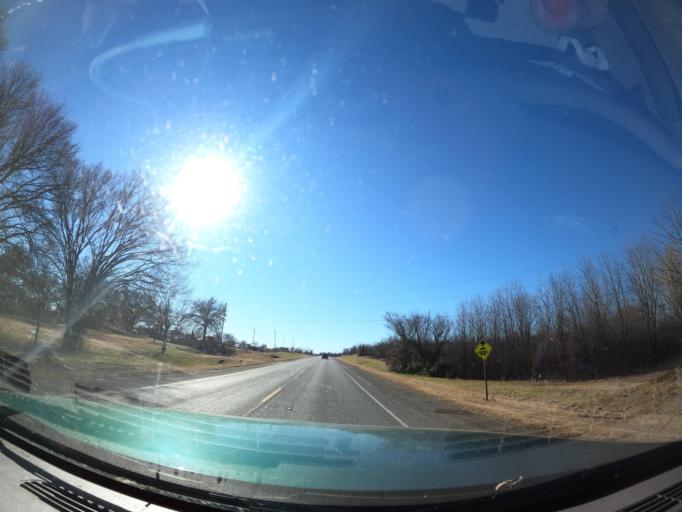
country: US
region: Oklahoma
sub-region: Muskogee County
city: Haskell
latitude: 35.8709
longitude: -95.6694
